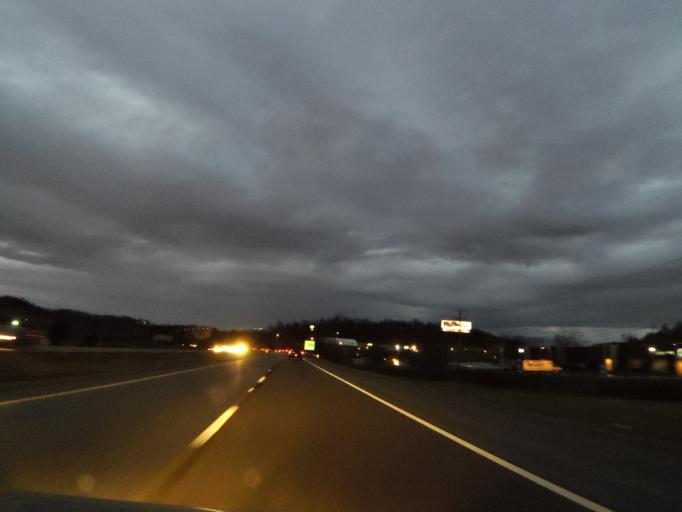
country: US
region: Tennessee
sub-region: Sullivan County
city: Colonial Heights
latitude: 36.4445
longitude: -82.5217
